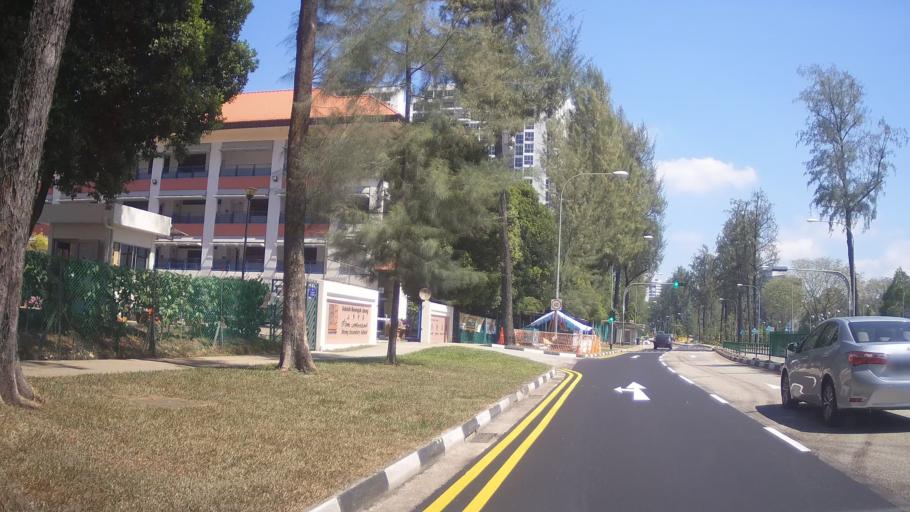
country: SG
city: Singapore
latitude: 1.3298
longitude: 103.7246
